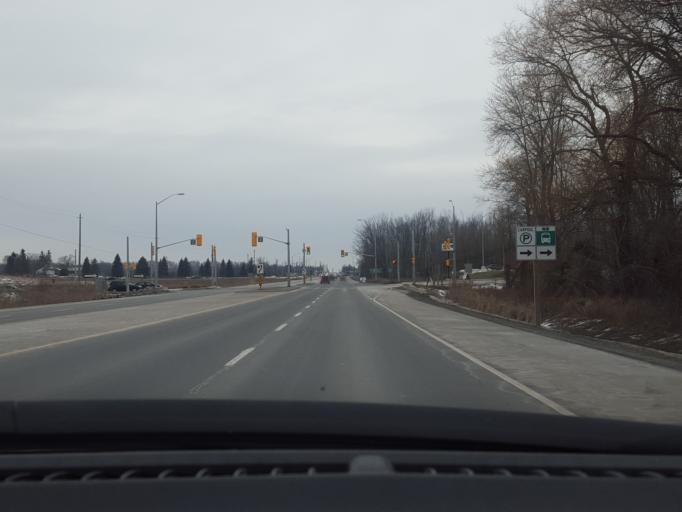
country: CA
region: Ontario
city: Keswick
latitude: 44.1903
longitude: -79.4375
